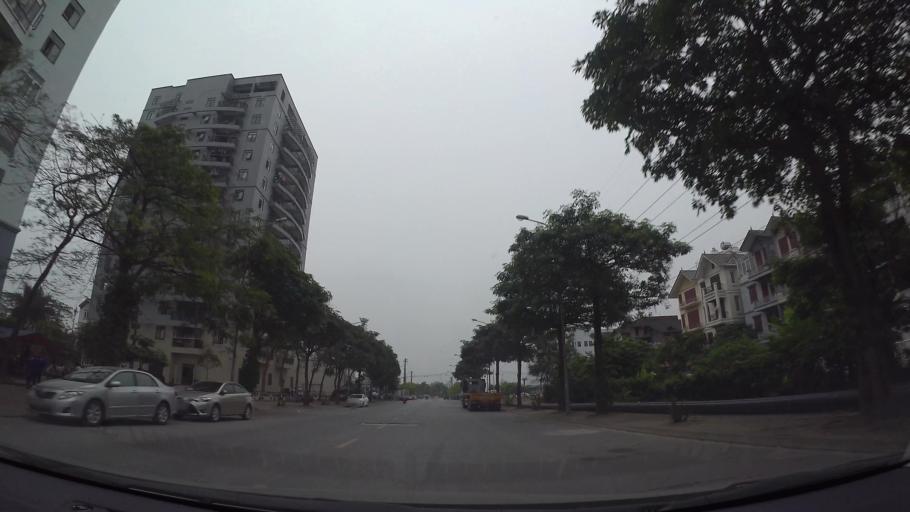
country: VN
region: Ha Noi
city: Trau Quy
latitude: 21.0359
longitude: 105.9063
